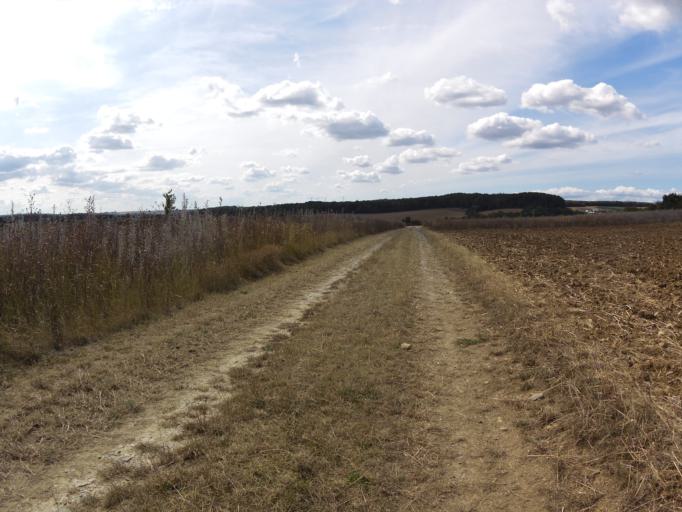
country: DE
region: Bavaria
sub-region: Regierungsbezirk Unterfranken
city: Guntersleben
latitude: 49.8582
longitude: 9.9146
